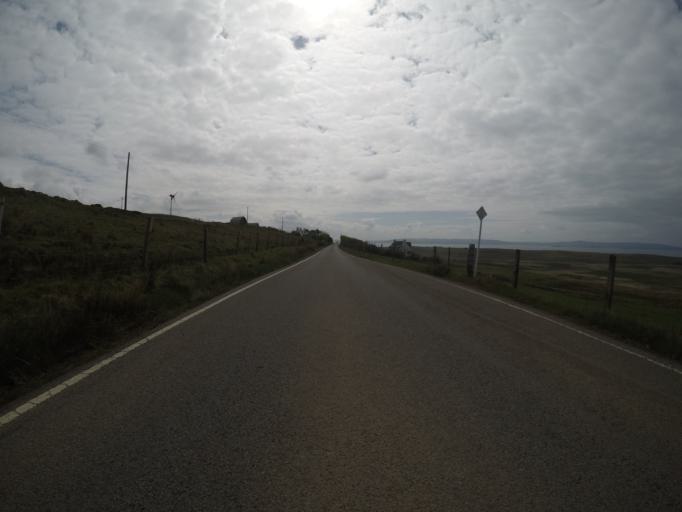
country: GB
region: Scotland
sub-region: Highland
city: Portree
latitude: 57.6341
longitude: -6.3768
